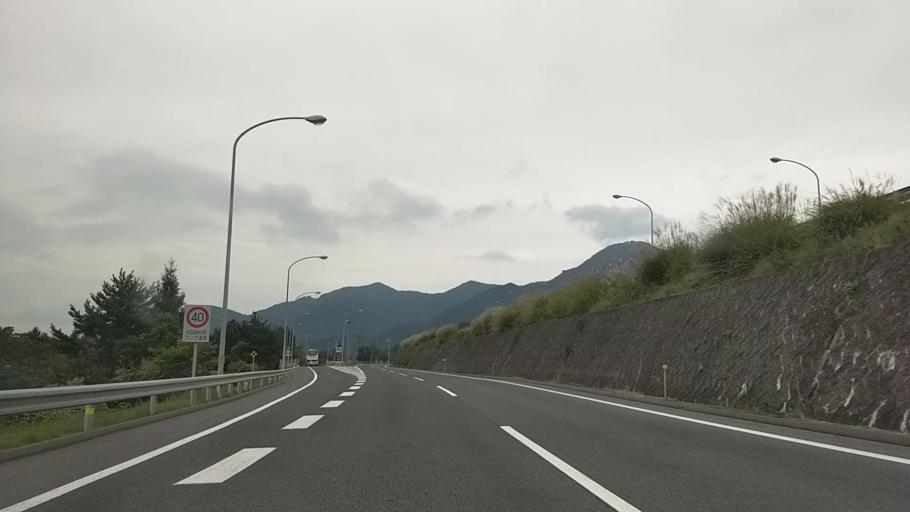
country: JP
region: Nagano
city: Nagano-shi
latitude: 36.4995
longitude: 138.0947
